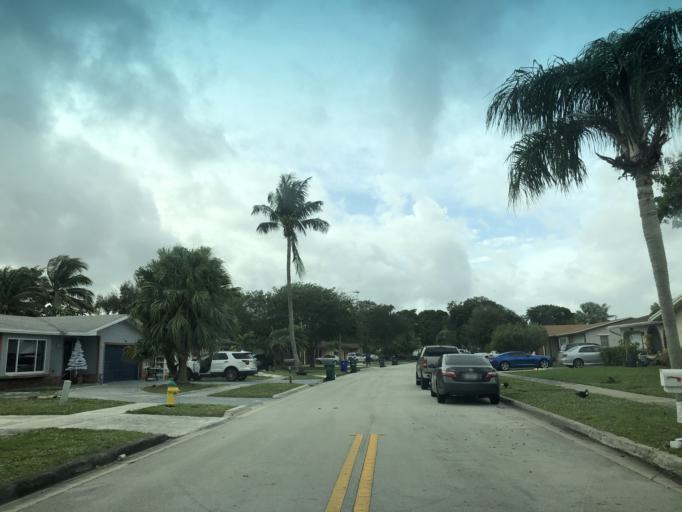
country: US
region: Florida
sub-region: Broward County
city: North Lauderdale
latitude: 26.2385
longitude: -80.2316
